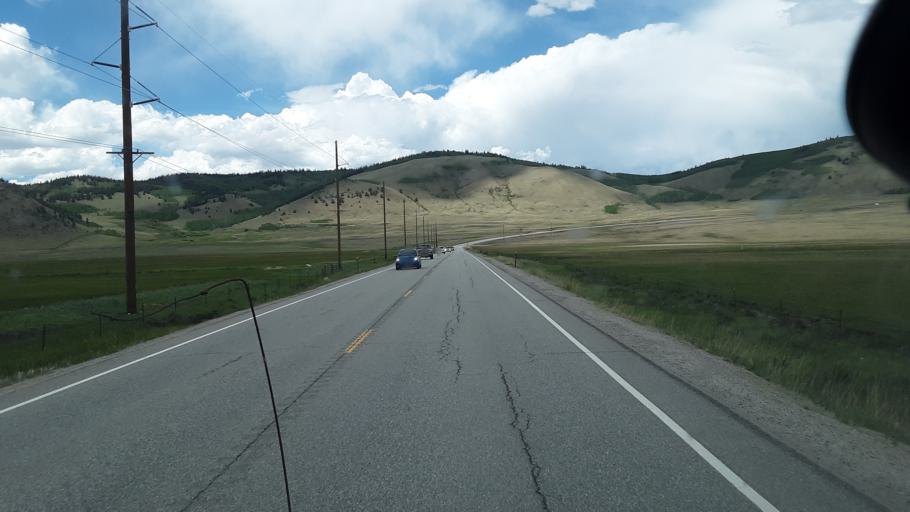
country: US
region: Colorado
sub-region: Summit County
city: Breckenridge
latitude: 39.3978
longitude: -105.7832
